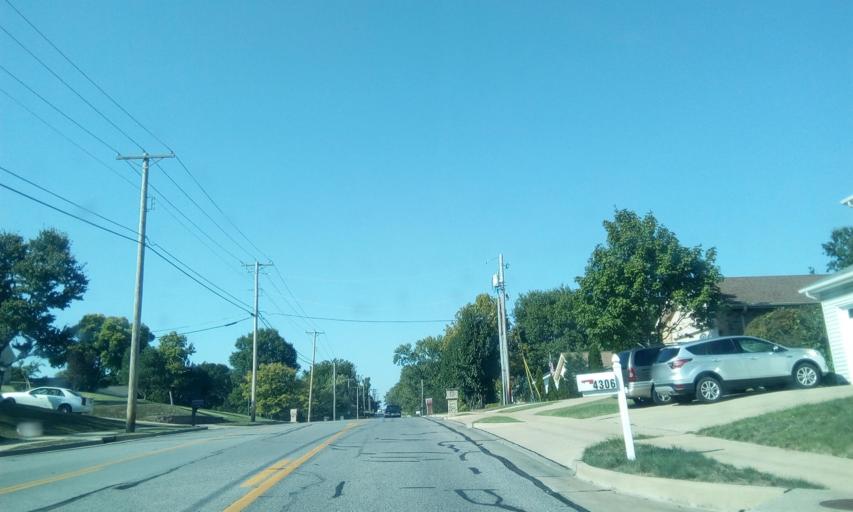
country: US
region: Missouri
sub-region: Saint Louis County
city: Green Park
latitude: 38.5082
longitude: -90.3428
